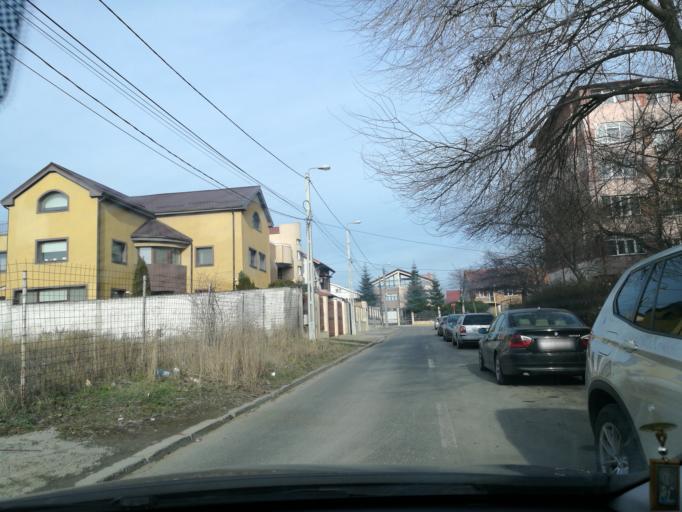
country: RO
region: Constanta
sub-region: Municipiul Constanta
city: Constanta
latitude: 44.1791
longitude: 28.6134
